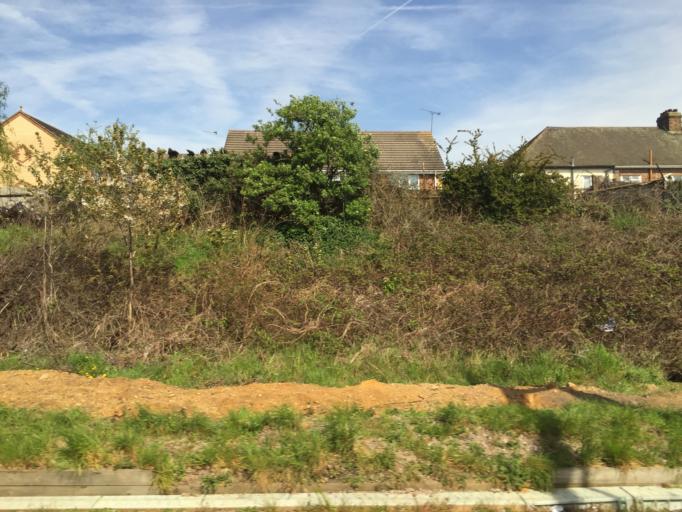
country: GB
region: England
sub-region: Greater London
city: Chadwell Heath
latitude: 51.5674
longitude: 0.1245
